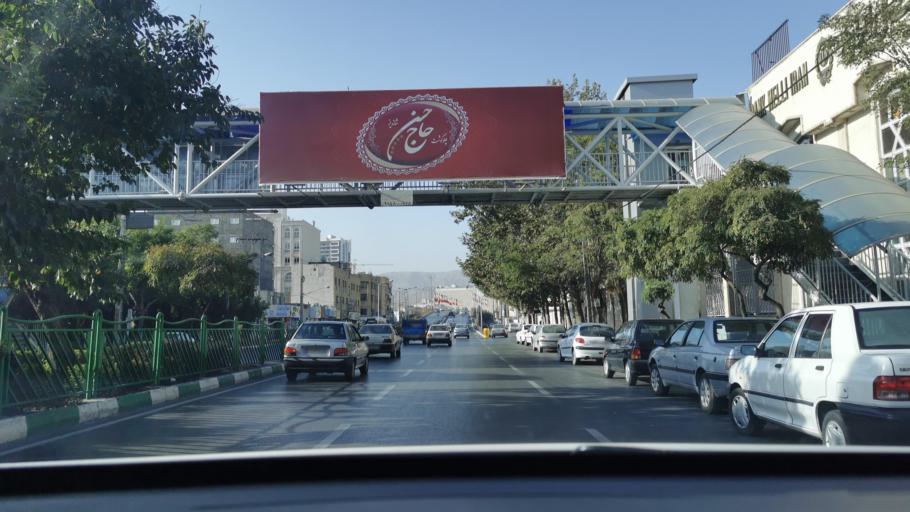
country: IR
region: Razavi Khorasan
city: Mashhad
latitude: 36.3304
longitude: 59.5029
